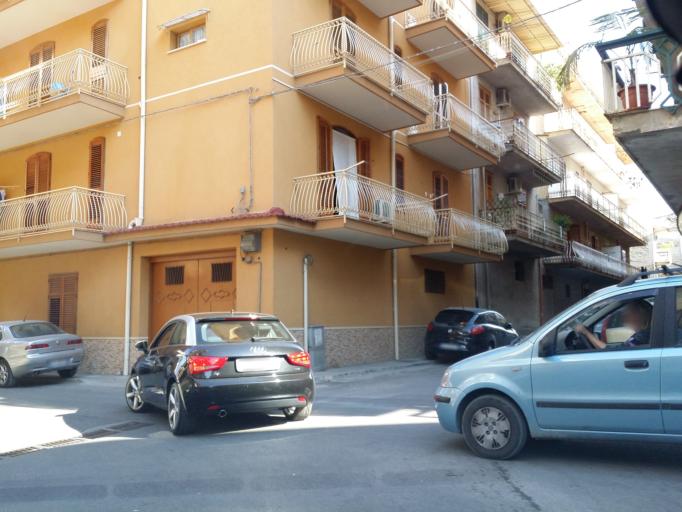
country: IT
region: Sicily
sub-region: Palermo
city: Misilmeri
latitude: 38.0302
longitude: 13.4466
